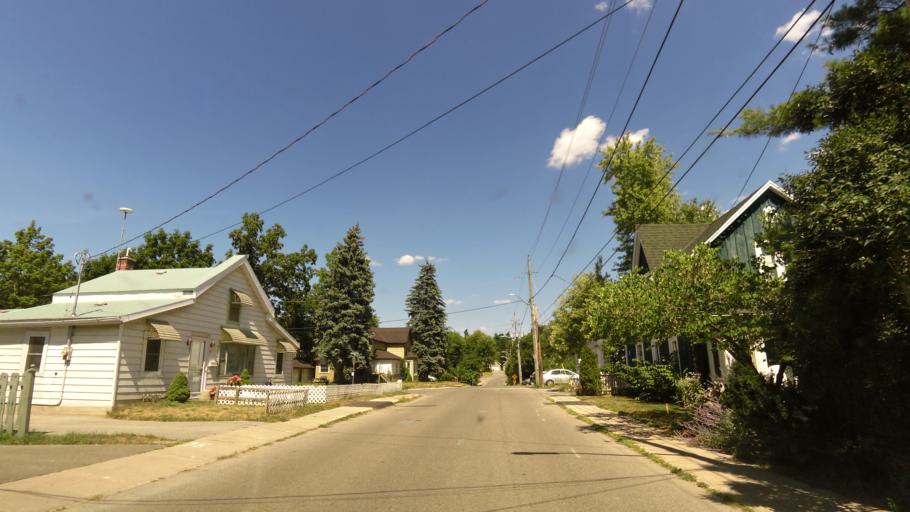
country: CA
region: Ontario
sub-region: Halton
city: Milton
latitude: 43.6525
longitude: -79.9237
